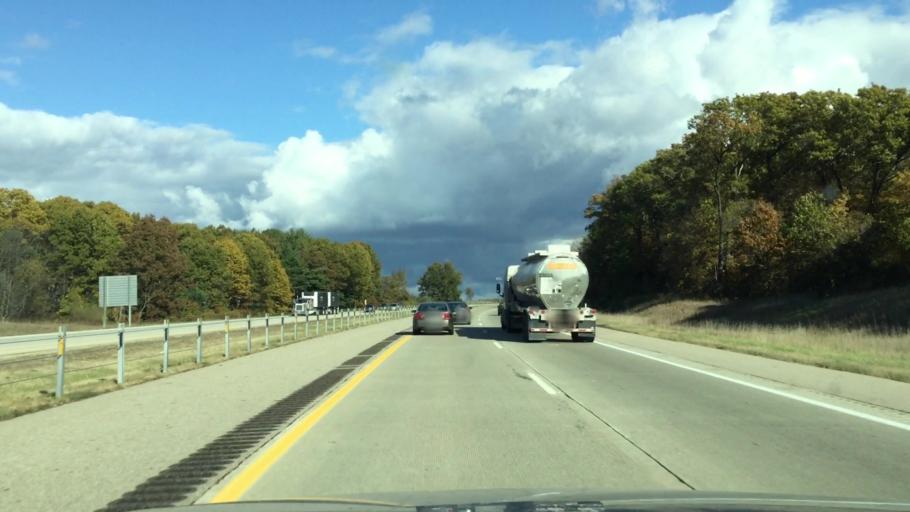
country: US
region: Michigan
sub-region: Van Buren County
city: Paw Paw
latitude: 42.2166
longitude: -85.8584
